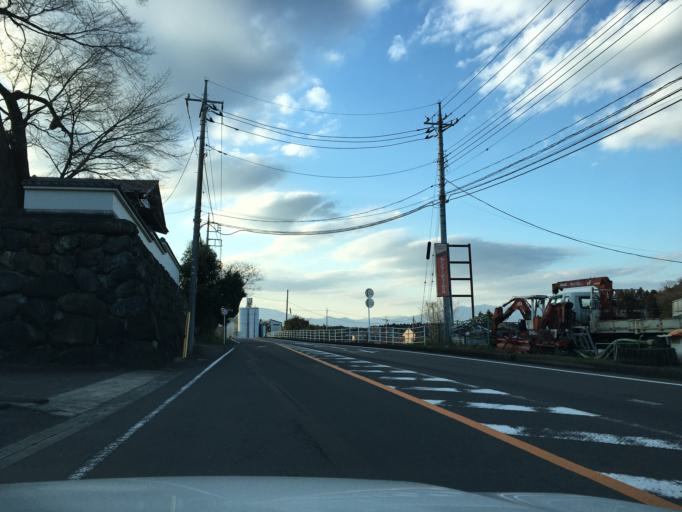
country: JP
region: Tochigi
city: Otawara
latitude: 36.8653
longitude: 140.0820
